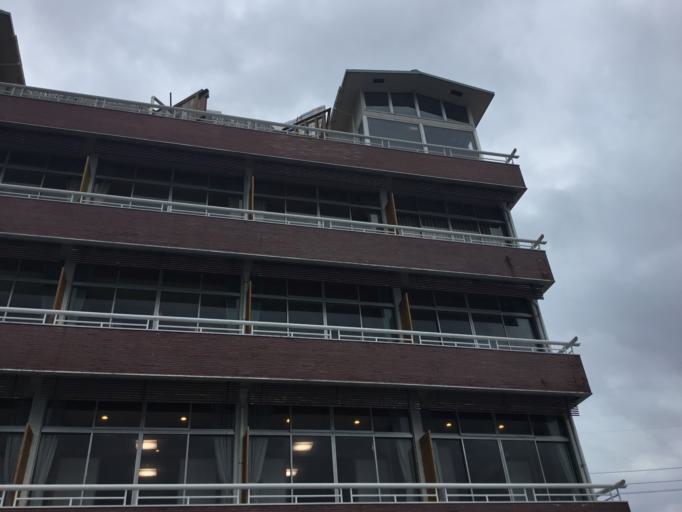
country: JP
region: Wakayama
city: Minato
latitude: 34.2746
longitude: 135.0672
